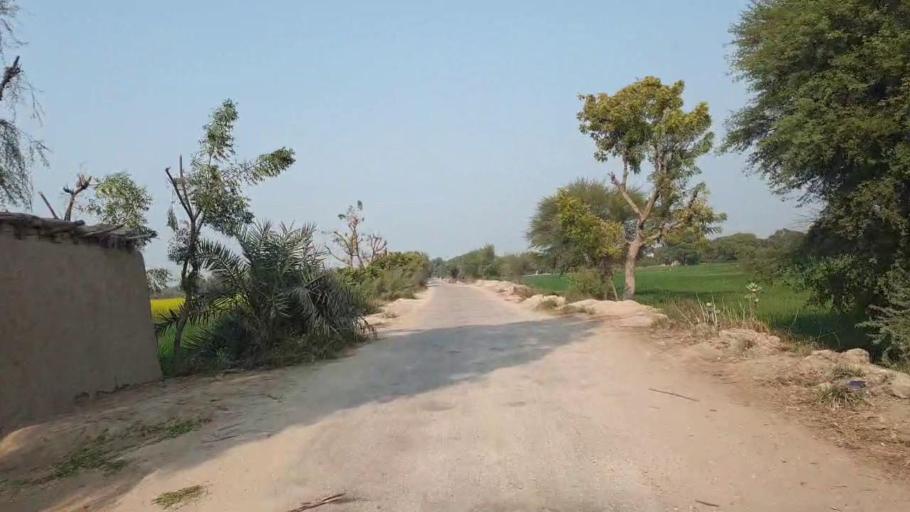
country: PK
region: Sindh
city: Hala
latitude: 25.8409
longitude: 68.4610
